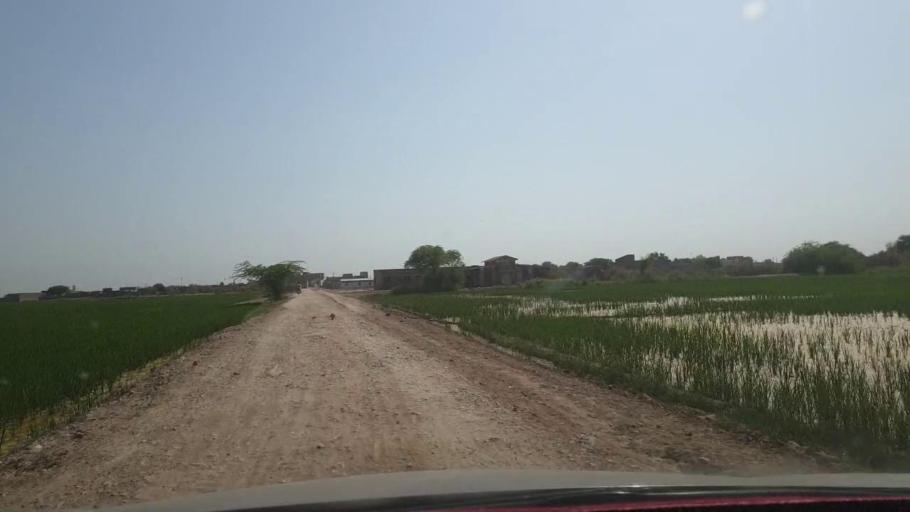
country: PK
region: Sindh
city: Nasirabad
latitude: 27.3491
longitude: 67.8424
